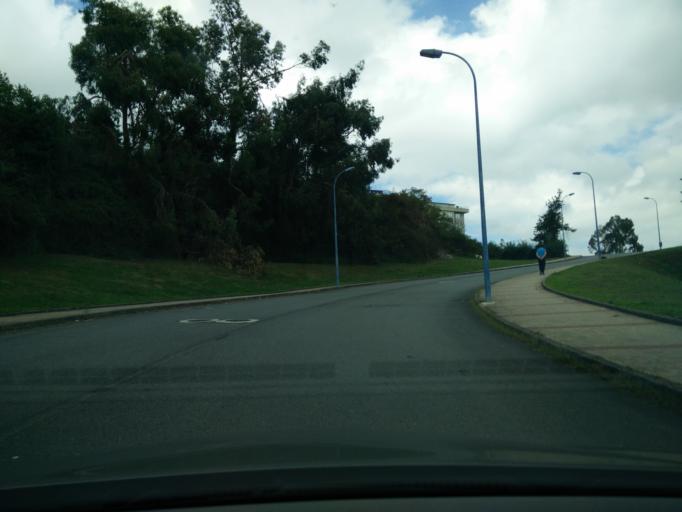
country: ES
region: Galicia
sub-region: Provincia da Coruna
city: Culleredo
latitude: 43.3199
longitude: -8.3812
